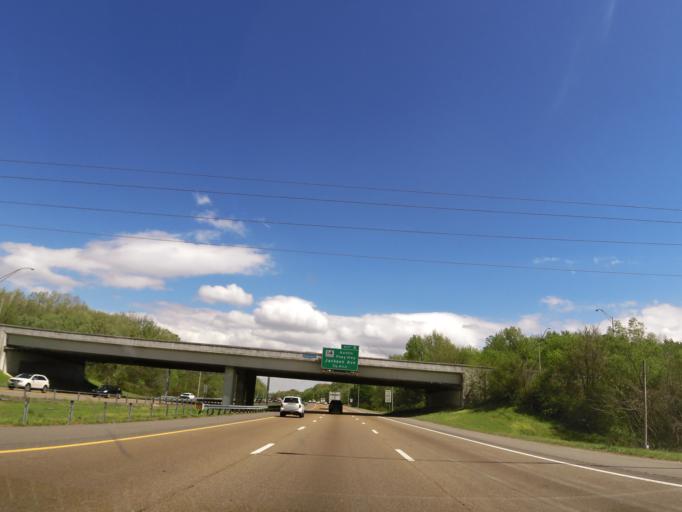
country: US
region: Tennessee
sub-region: Shelby County
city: Bartlett
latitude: 35.1898
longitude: -89.9458
